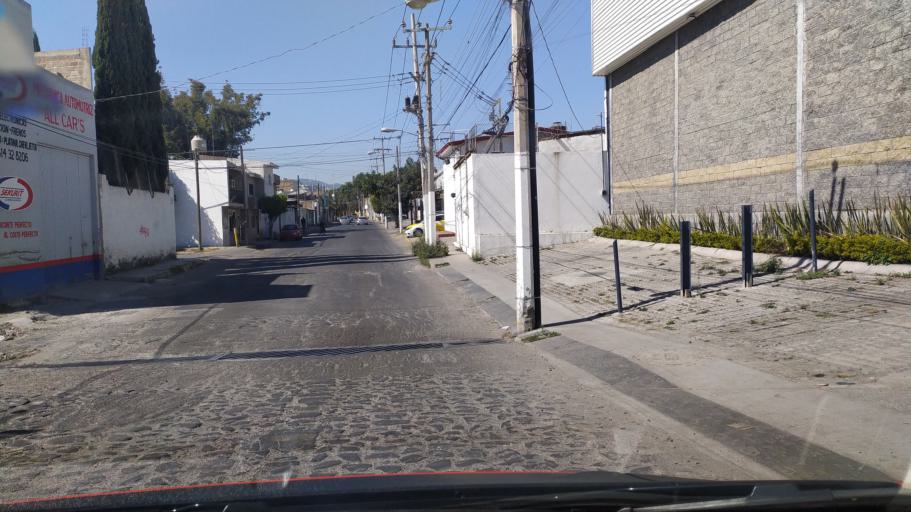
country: MX
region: Jalisco
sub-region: Tlajomulco de Zuniga
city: Palomar
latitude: 20.6289
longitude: -103.4374
